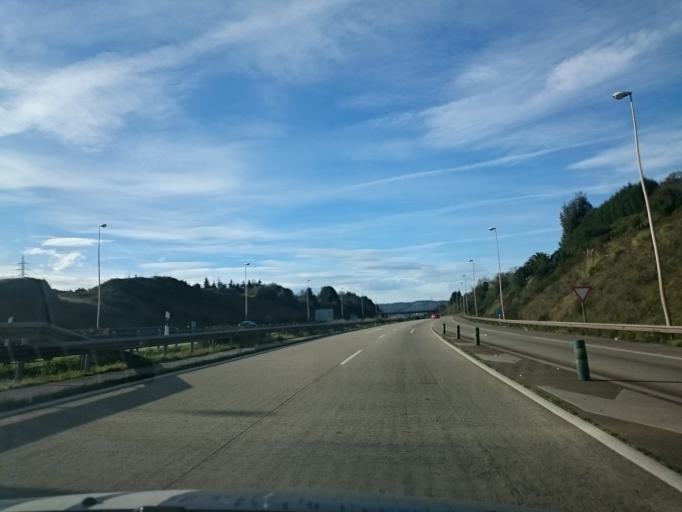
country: ES
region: Asturias
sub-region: Province of Asturias
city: Natahoyo
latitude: 43.5185
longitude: -5.7090
